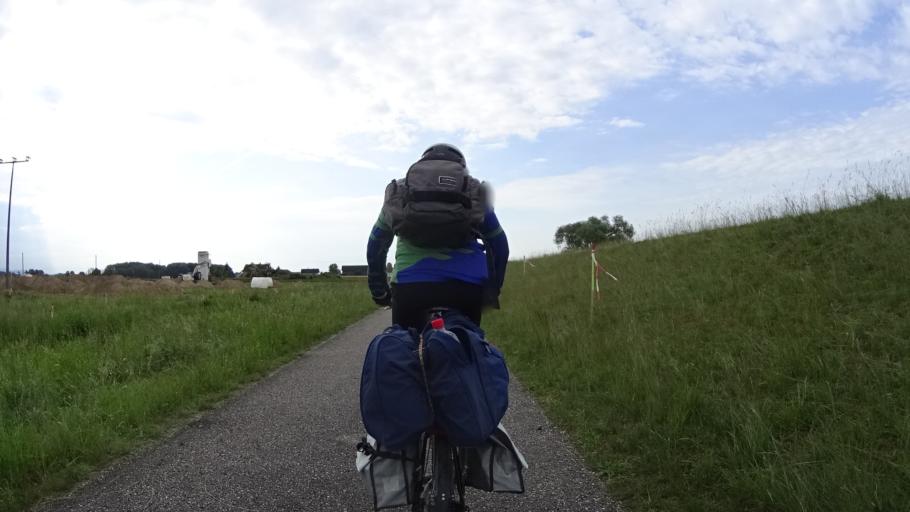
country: DE
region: Bavaria
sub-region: Lower Bavaria
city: Irlbach
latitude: 48.8676
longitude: 12.7596
